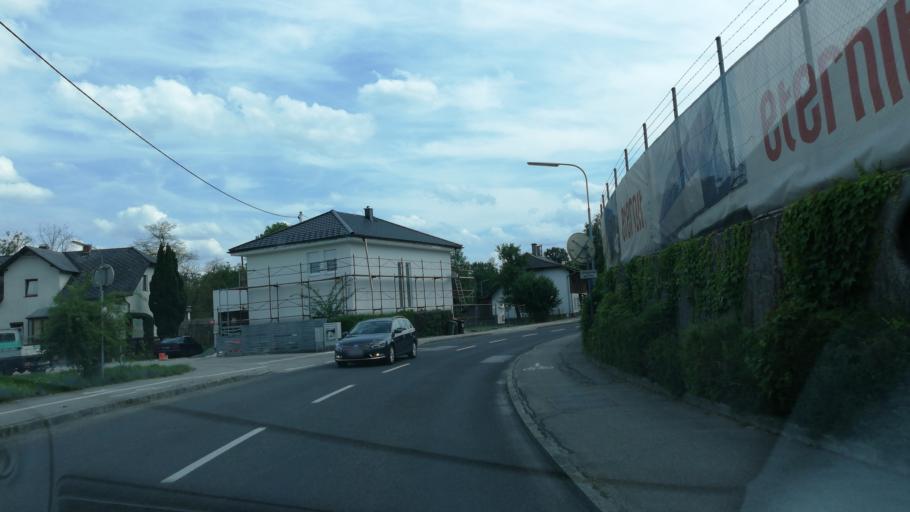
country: AT
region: Upper Austria
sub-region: Politischer Bezirk Vocklabruck
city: Vocklabruck
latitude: 48.0000
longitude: 13.6636
